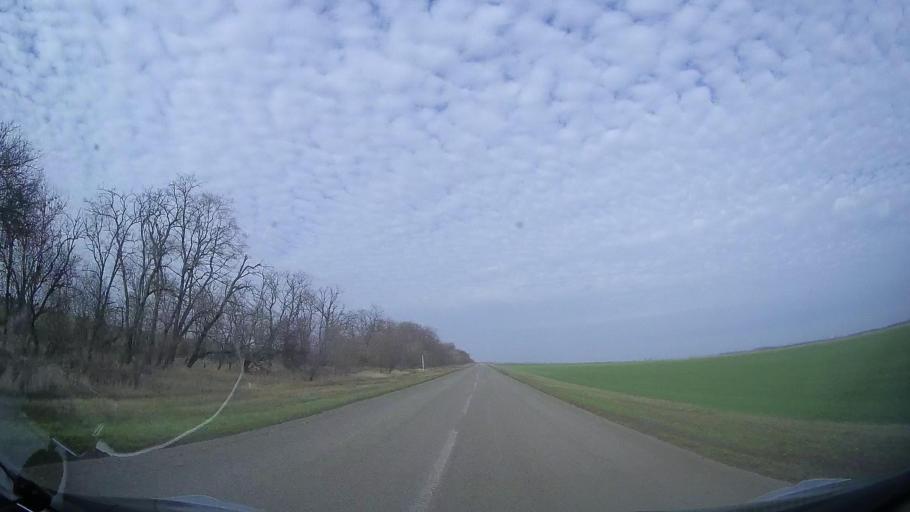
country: RU
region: Rostov
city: Gigant
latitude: 46.9297
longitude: 41.2452
